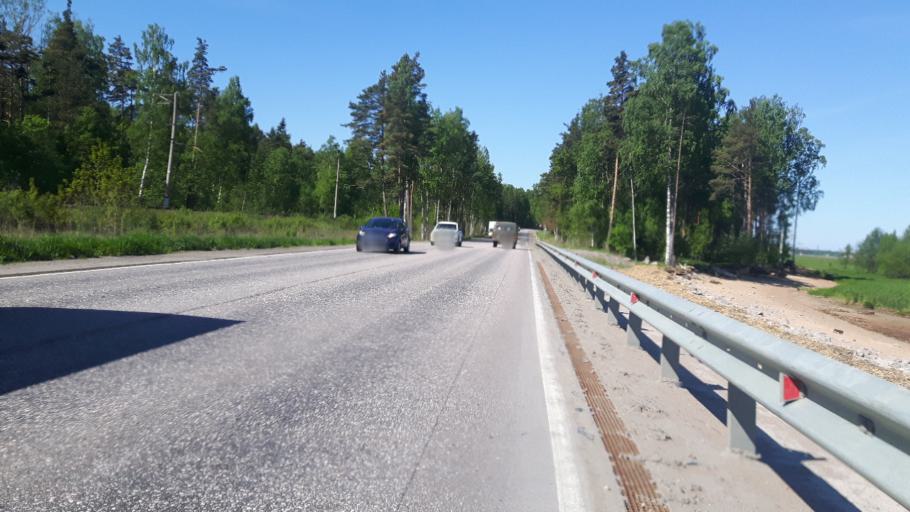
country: RU
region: Leningrad
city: Lebyazh'ye
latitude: 59.9566
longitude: 29.4769
